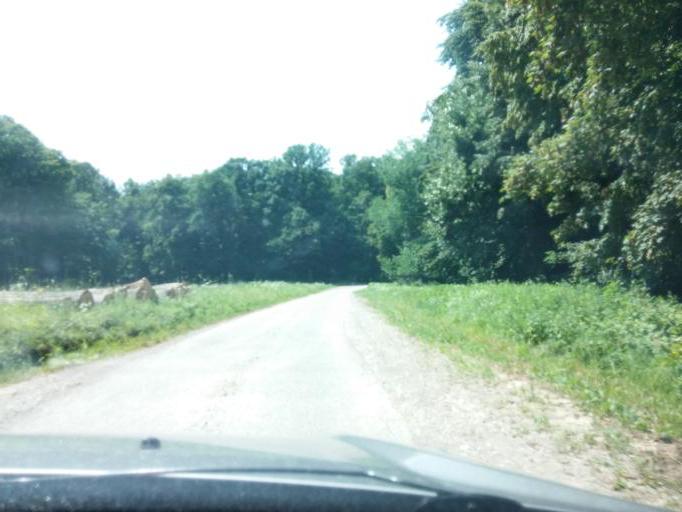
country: HU
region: Somogy
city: Kaposvar
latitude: 46.2546
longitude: 17.8035
